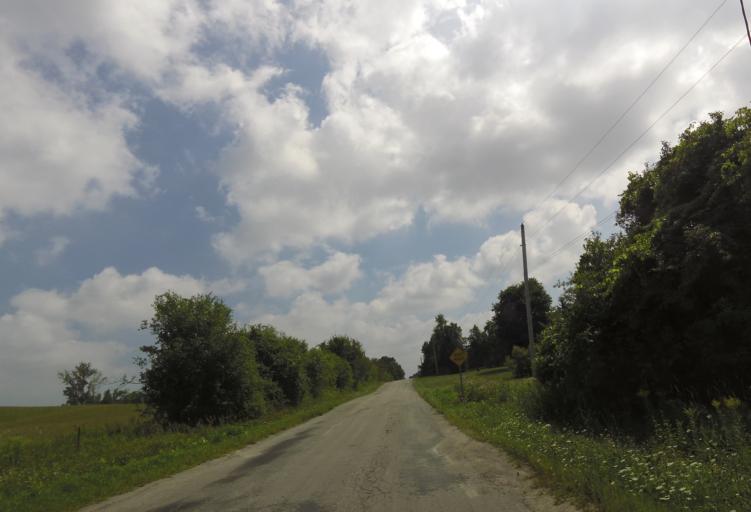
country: CA
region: Ontario
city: Oshawa
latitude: 43.9970
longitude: -78.8747
